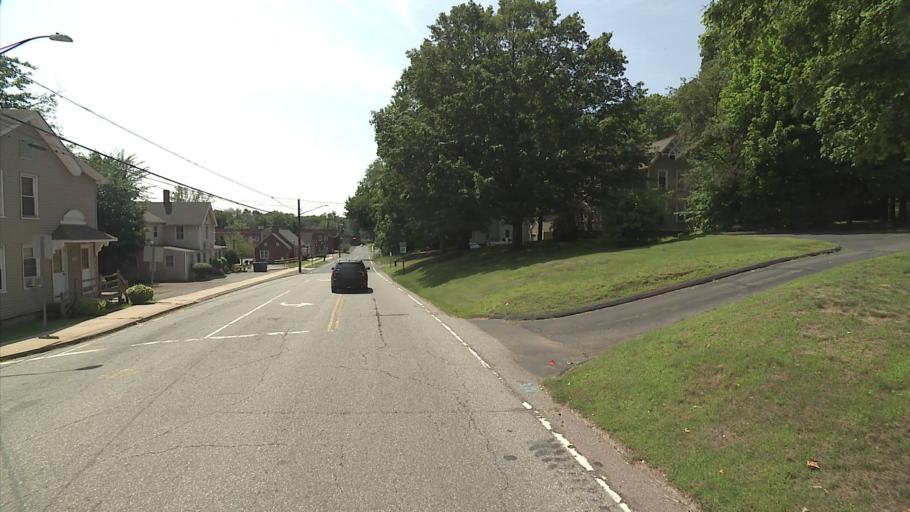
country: US
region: Connecticut
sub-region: Hartford County
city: Kensington
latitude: 41.6354
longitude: -72.7688
